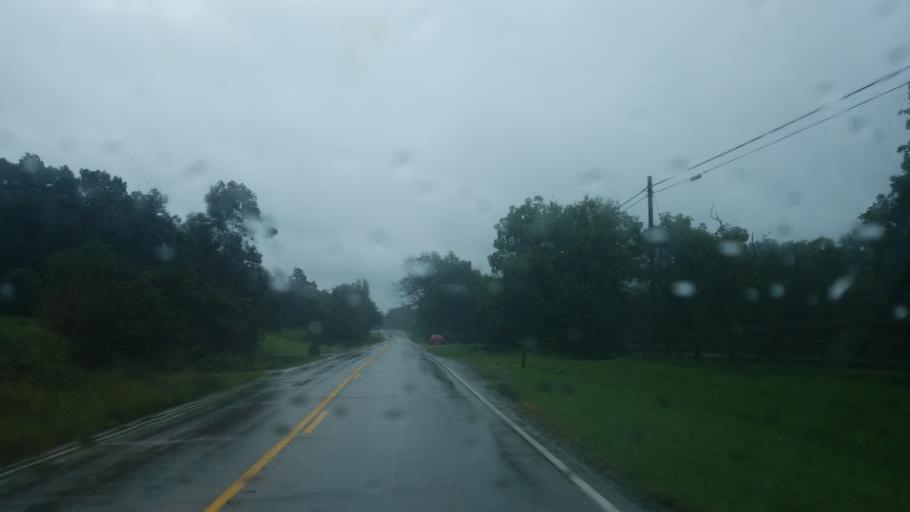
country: US
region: Kentucky
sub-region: Fleming County
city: Flemingsburg
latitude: 38.3405
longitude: -83.5981
